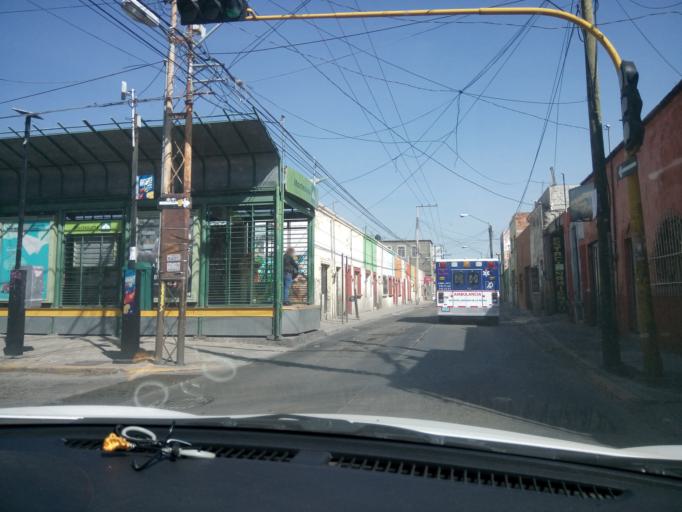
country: MX
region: Guanajuato
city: Leon
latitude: 21.1304
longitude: -101.6793
